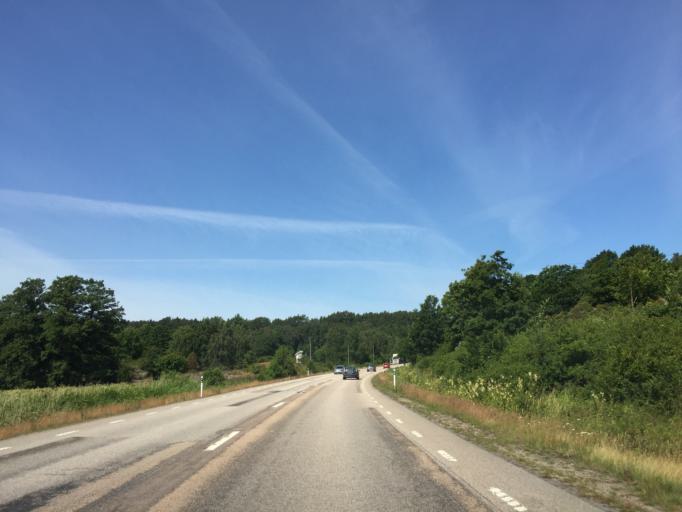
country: SE
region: Vaestra Goetaland
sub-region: Lysekils Kommun
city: Lysekil
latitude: 58.3034
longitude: 11.4948
